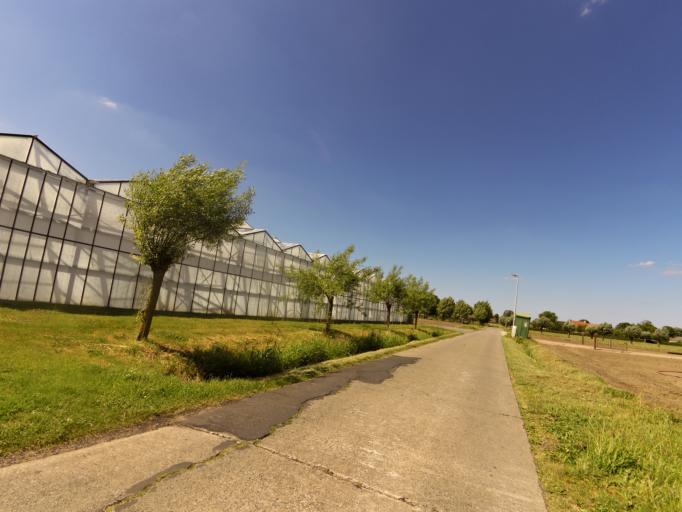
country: BE
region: Flanders
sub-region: Provincie West-Vlaanderen
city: Jabbeke
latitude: 51.1738
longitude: 3.0973
